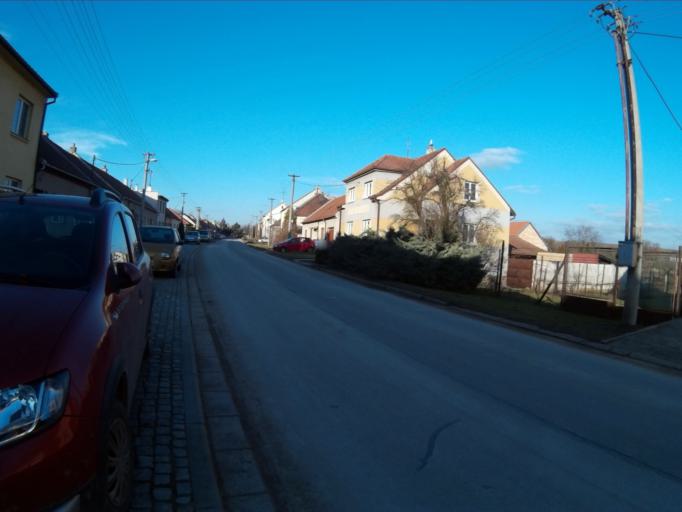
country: CZ
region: South Moravian
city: Krenovice
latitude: 49.1459
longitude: 16.8272
